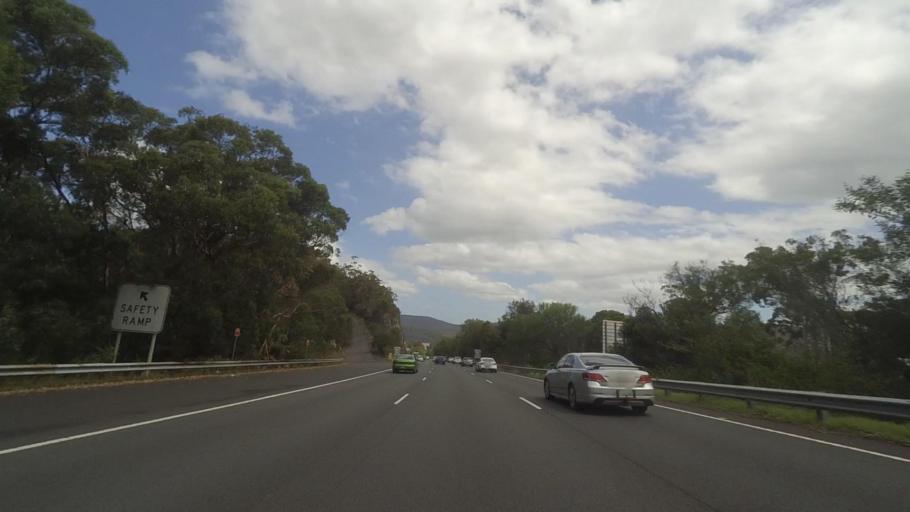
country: AU
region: New South Wales
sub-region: Hornsby Shire
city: Berowra Heights
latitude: -33.5228
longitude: 151.1962
